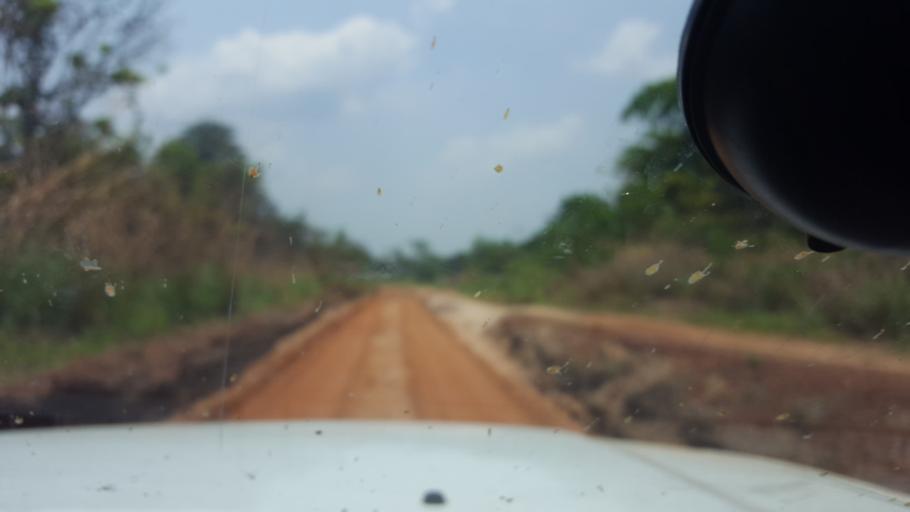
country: CD
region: Bandundu
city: Mushie
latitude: -3.7502
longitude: 16.6336
